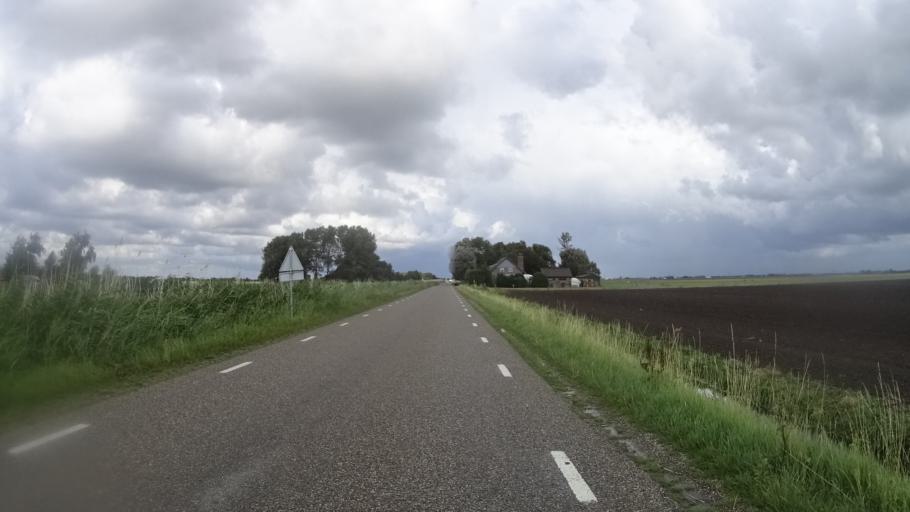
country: NL
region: North Holland
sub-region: Gemeente Schagen
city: Schagen
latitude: 52.8121
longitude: 4.7812
